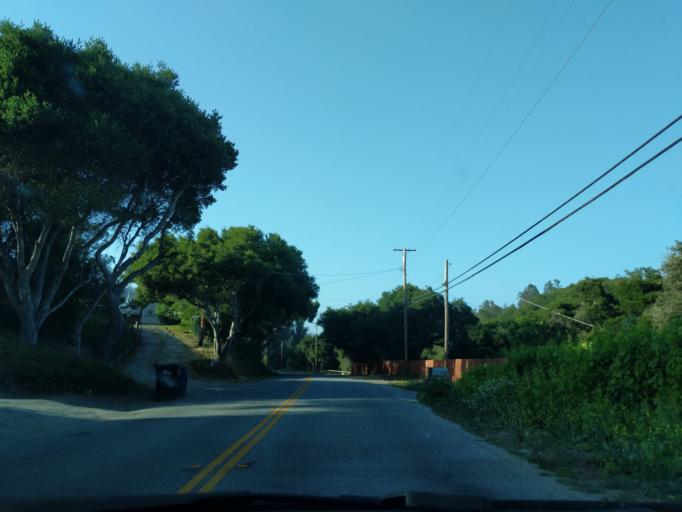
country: US
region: California
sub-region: Monterey County
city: Las Lomas
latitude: 36.8739
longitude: -121.6889
